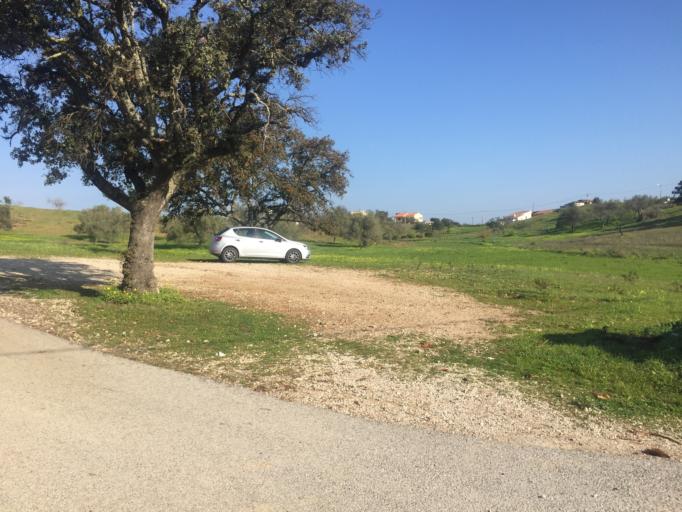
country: PT
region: Faro
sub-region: Vila Real de Santo Antonio
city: Monte Gordo
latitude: 37.2211
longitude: -7.5630
